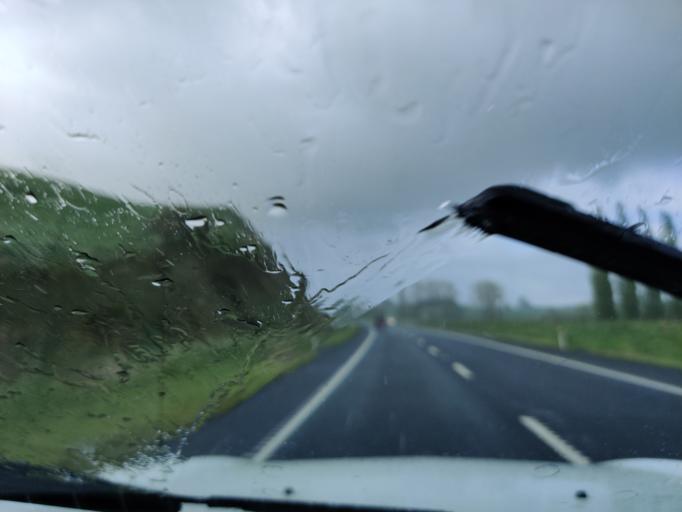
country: NZ
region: Waikato
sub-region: Matamata-Piako District
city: Matamata
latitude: -37.9684
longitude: 175.6902
